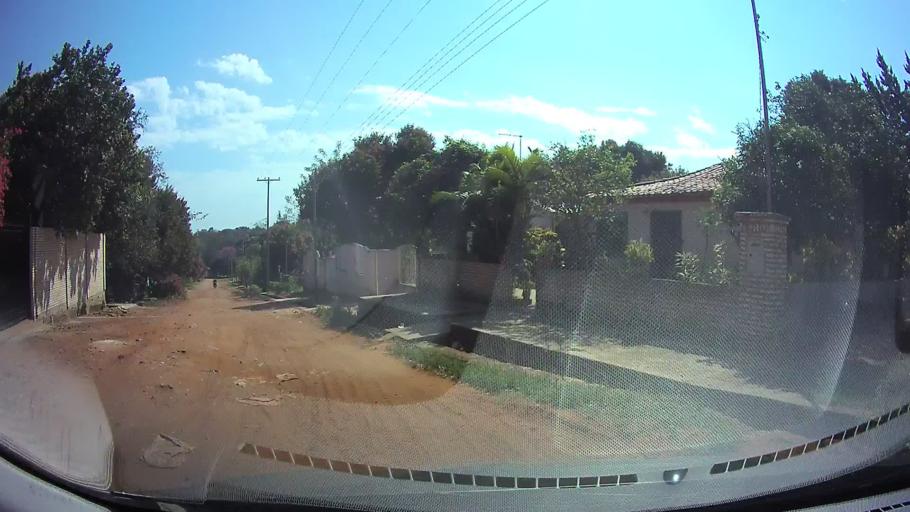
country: PY
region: Central
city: Limpio
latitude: -25.2303
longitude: -57.4396
